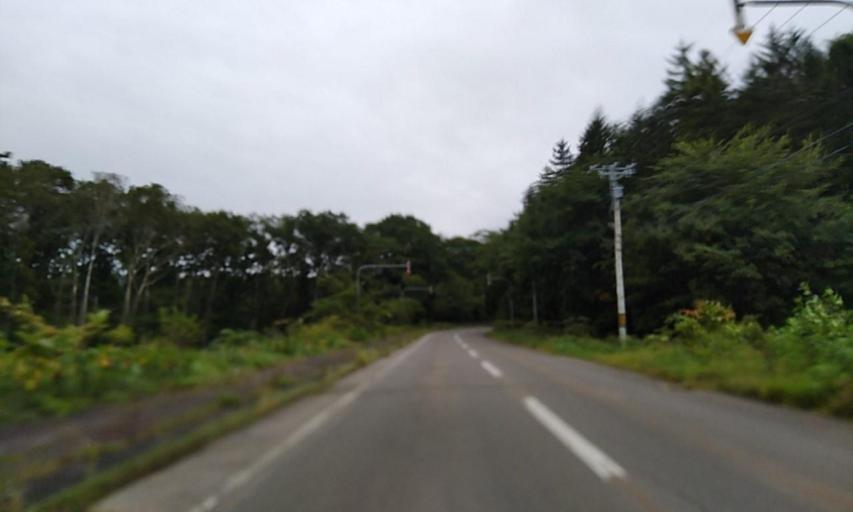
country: JP
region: Hokkaido
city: Obihiro
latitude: 42.6757
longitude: 143.0419
